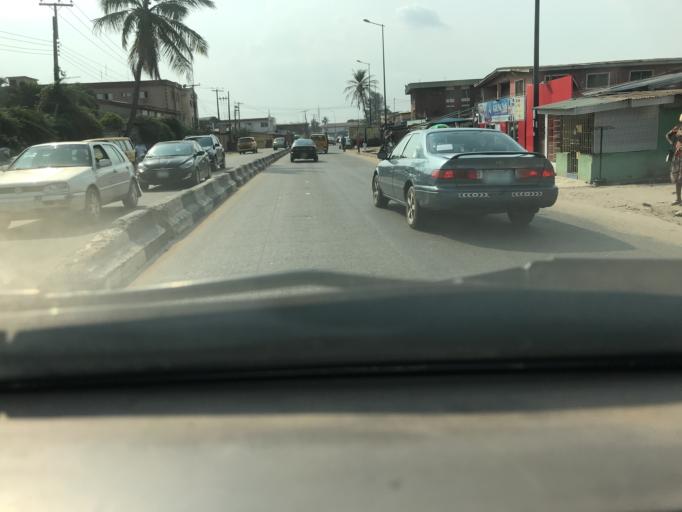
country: NG
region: Lagos
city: Agege
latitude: 6.6022
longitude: 3.3045
